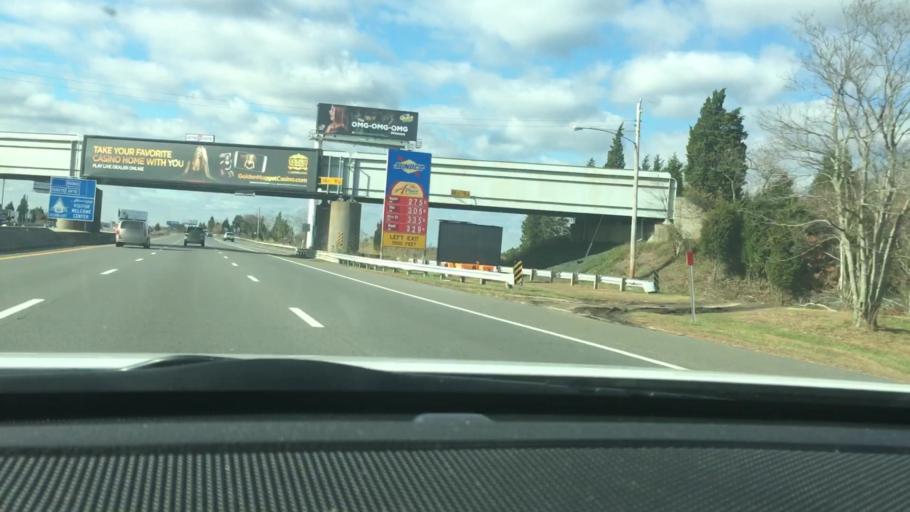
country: US
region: New Jersey
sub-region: Atlantic County
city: Ventnor City
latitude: 39.3770
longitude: -74.4813
